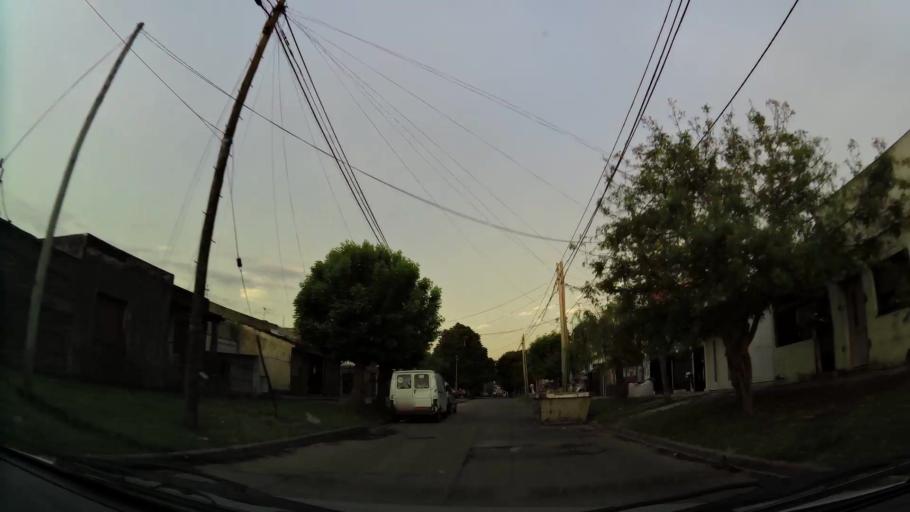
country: AR
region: Buenos Aires
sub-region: Partido de Lomas de Zamora
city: Lomas de Zamora
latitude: -34.7647
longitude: -58.3720
